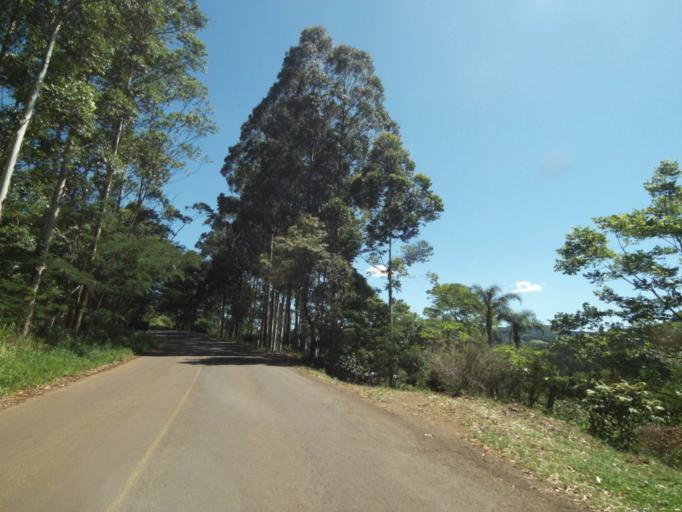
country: BR
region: Parana
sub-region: Ampere
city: Ampere
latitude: -26.1809
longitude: -53.3643
